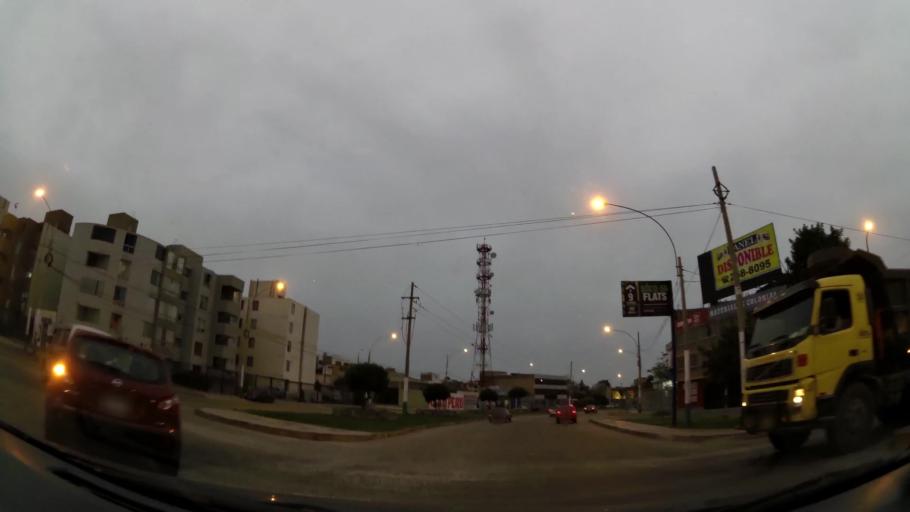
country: PE
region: Callao
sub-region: Callao
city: Callao
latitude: -12.0705
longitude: -77.1097
